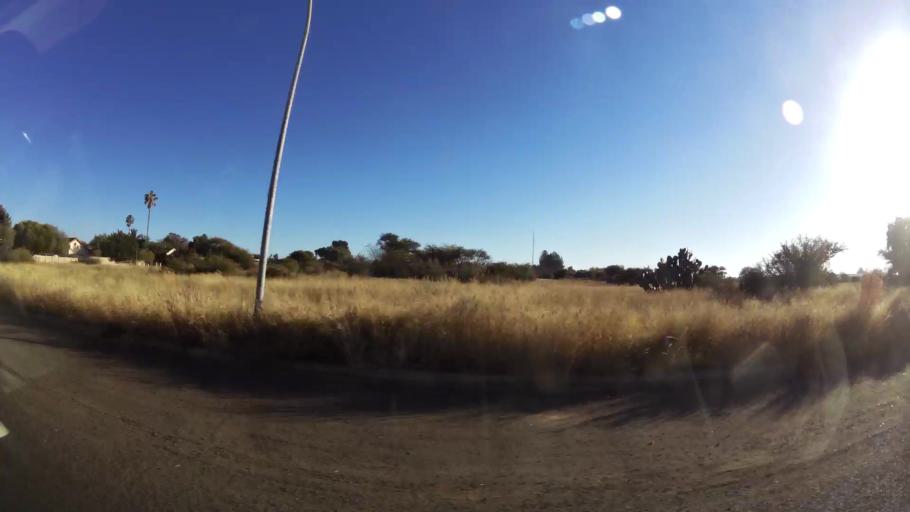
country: ZA
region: Northern Cape
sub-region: Frances Baard District Municipality
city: Kimberley
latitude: -28.7478
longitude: 24.7275
